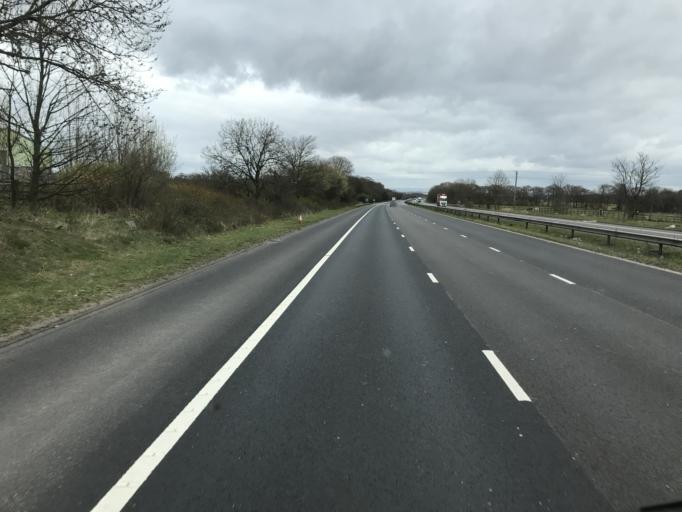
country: GB
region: England
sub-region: St. Helens
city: St Helens
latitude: 53.4101
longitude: -2.7067
